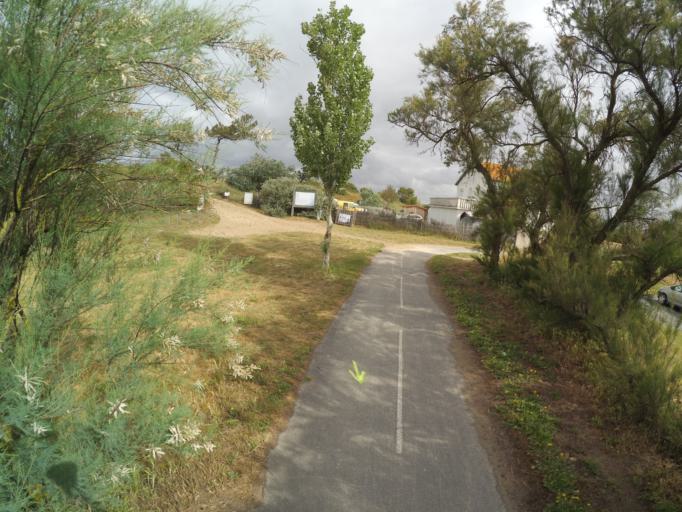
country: FR
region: Poitou-Charentes
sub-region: Departement de la Charente-Maritime
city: Aytre
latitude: 46.1183
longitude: -1.1235
